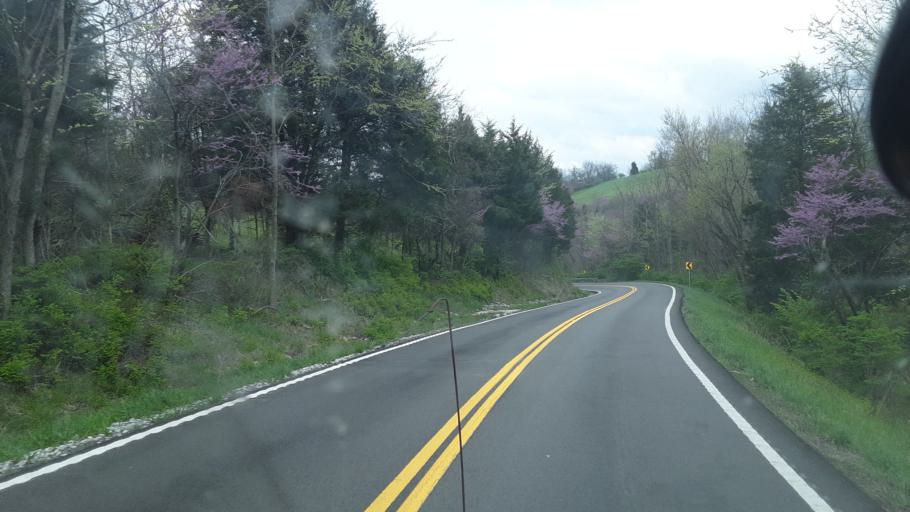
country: US
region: Kentucky
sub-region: Grant County
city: Dry Ridge
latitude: 38.6535
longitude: -84.6802
